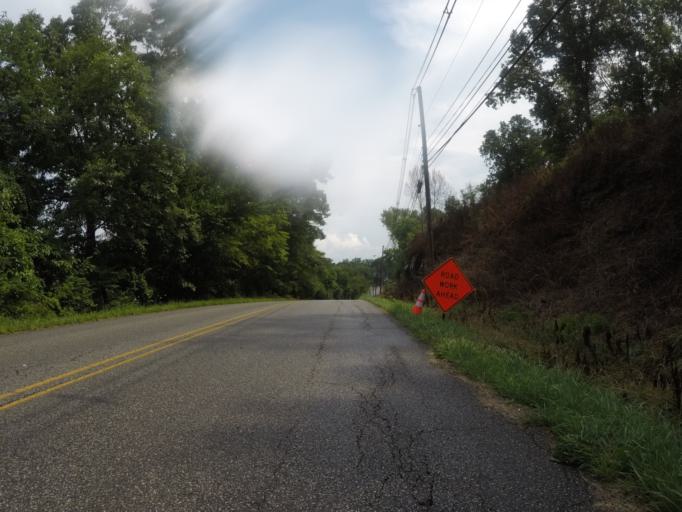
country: US
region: Kentucky
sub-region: Boyd County
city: Westwood
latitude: 38.4752
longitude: -82.6691
